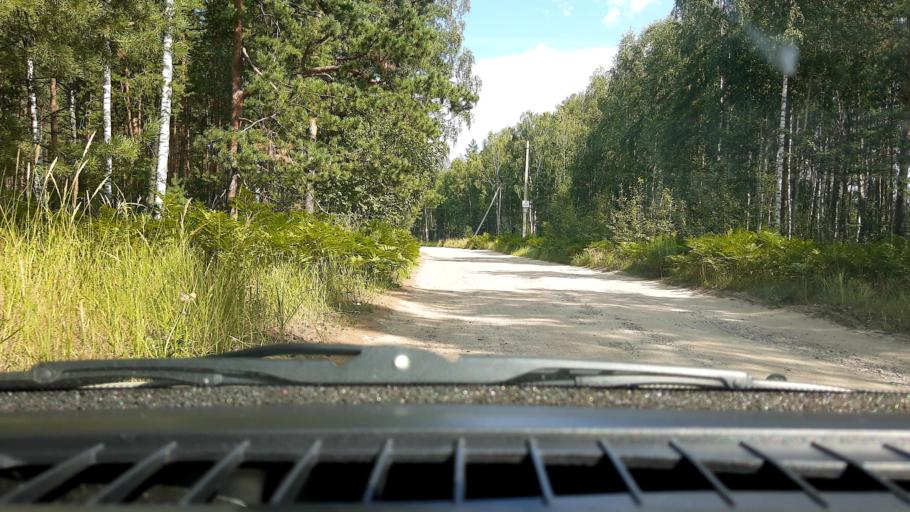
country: RU
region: Nizjnij Novgorod
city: Lukino
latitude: 56.3338
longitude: 43.6518
